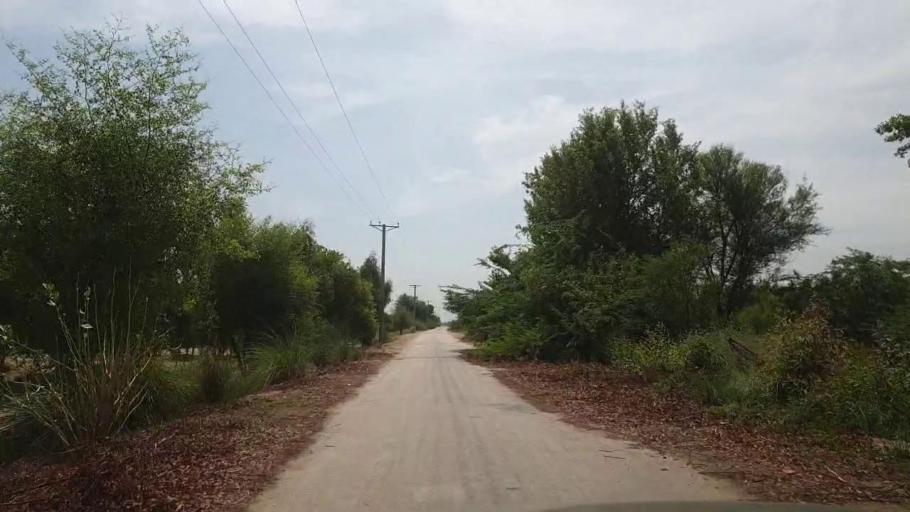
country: PK
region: Sindh
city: Kot Diji
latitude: 27.1192
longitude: 69.0049
